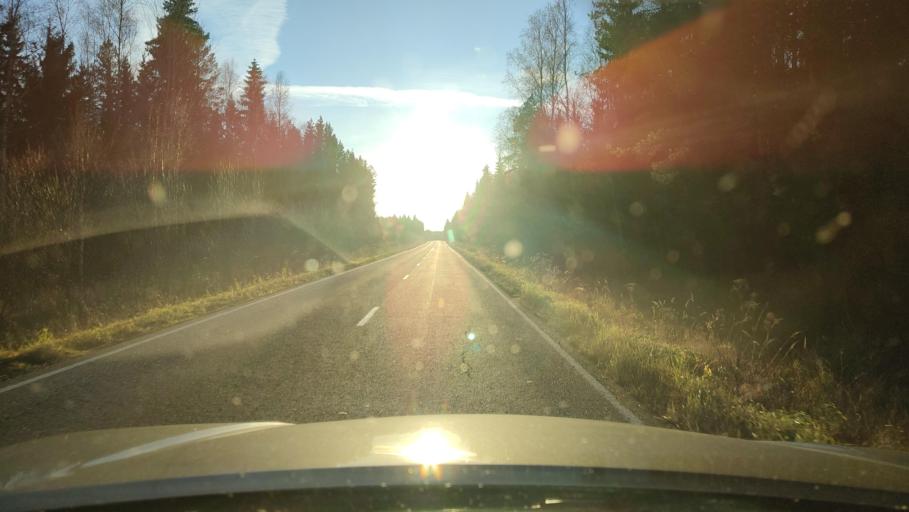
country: FI
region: Ostrobothnia
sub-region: Vaasa
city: Malax
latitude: 62.6955
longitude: 21.5678
